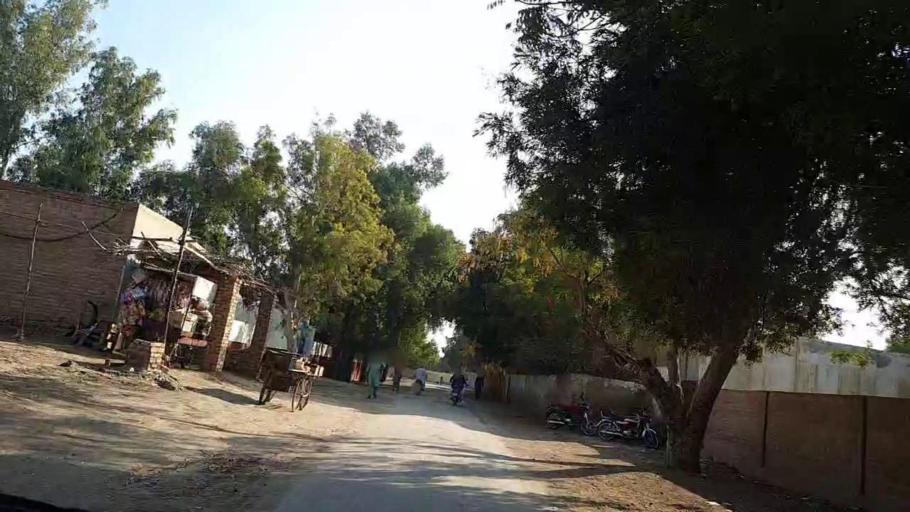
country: PK
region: Sindh
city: Sakrand
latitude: 26.1305
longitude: 68.2192
